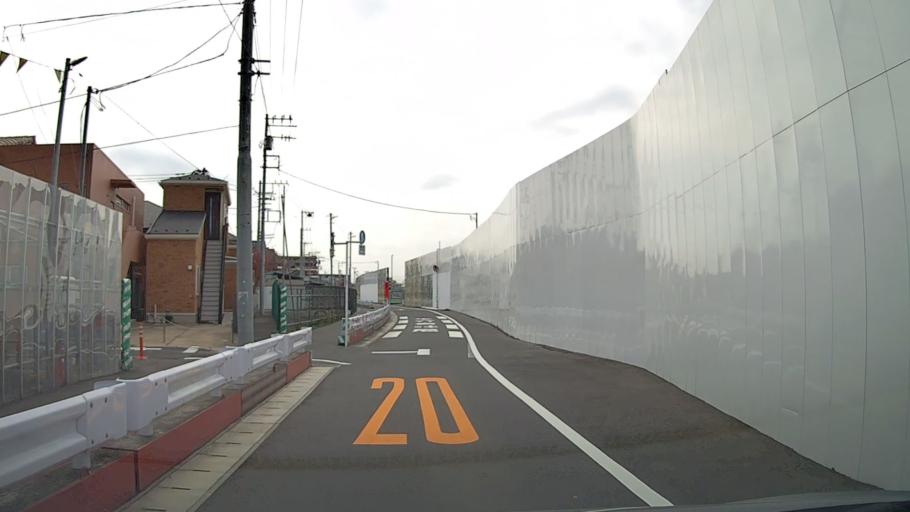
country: JP
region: Saitama
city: Wako
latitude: 35.7535
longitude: 139.5989
